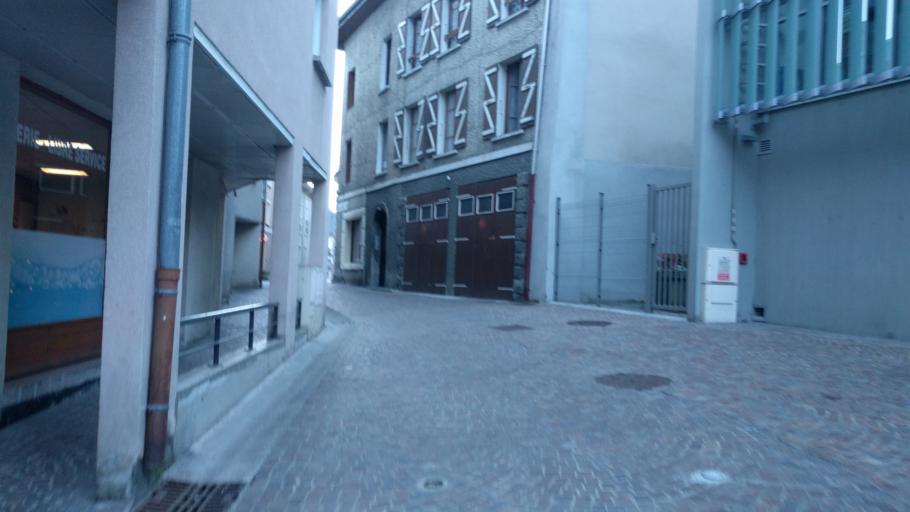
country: FR
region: Rhone-Alpes
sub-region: Departement de la Savoie
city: Saint-Jean-de-Maurienne
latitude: 45.2769
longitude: 6.3434
